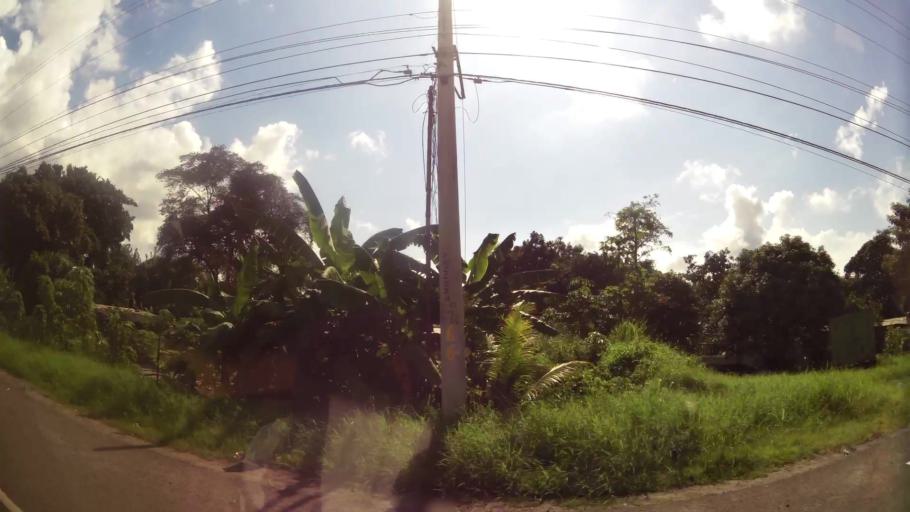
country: PA
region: Panama
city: Nuevo Arraijan
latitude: 8.9069
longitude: -79.7470
